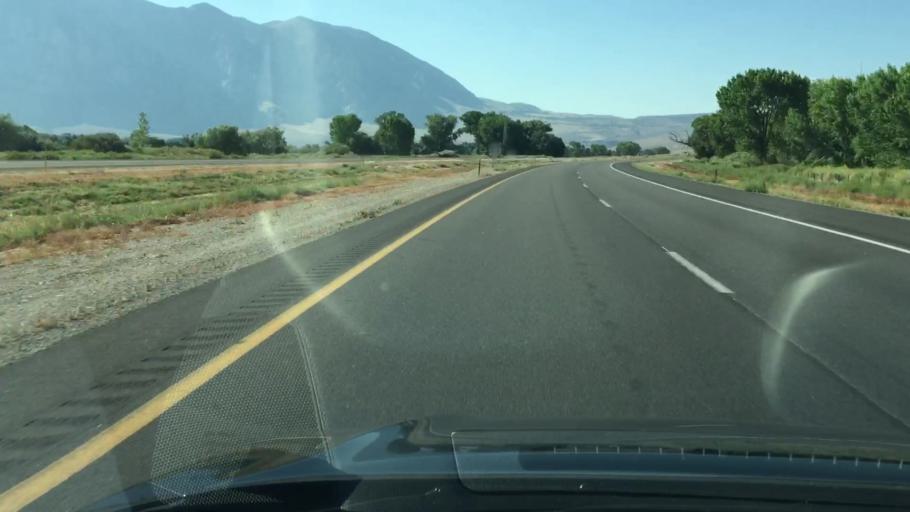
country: US
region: California
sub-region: Inyo County
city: West Bishop
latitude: 37.4104
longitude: -118.5499
